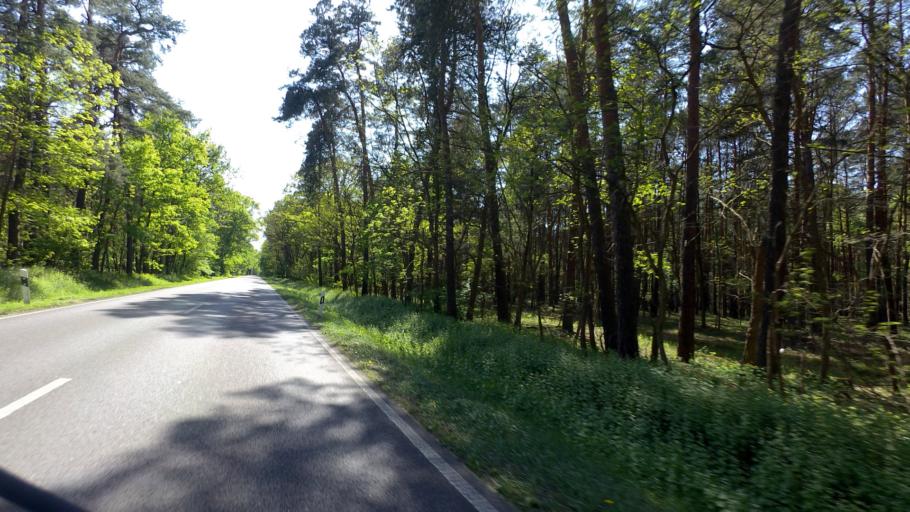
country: DE
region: Brandenburg
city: Tauche
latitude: 52.1422
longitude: 14.2079
